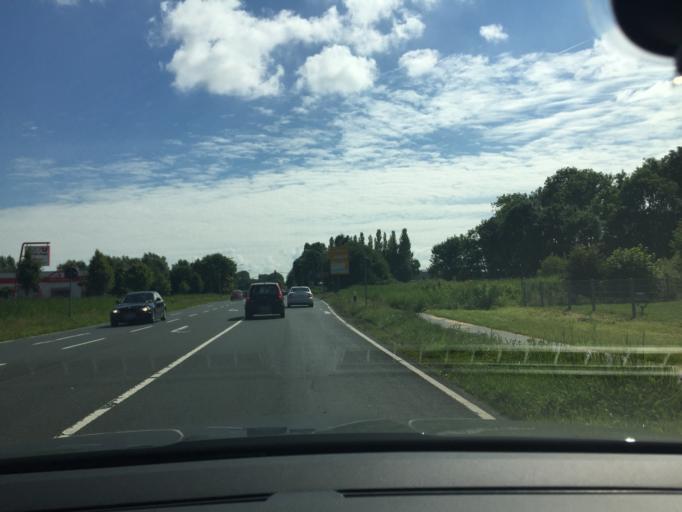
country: DE
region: Lower Saxony
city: Fedderwarden
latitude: 53.5266
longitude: 8.0663
